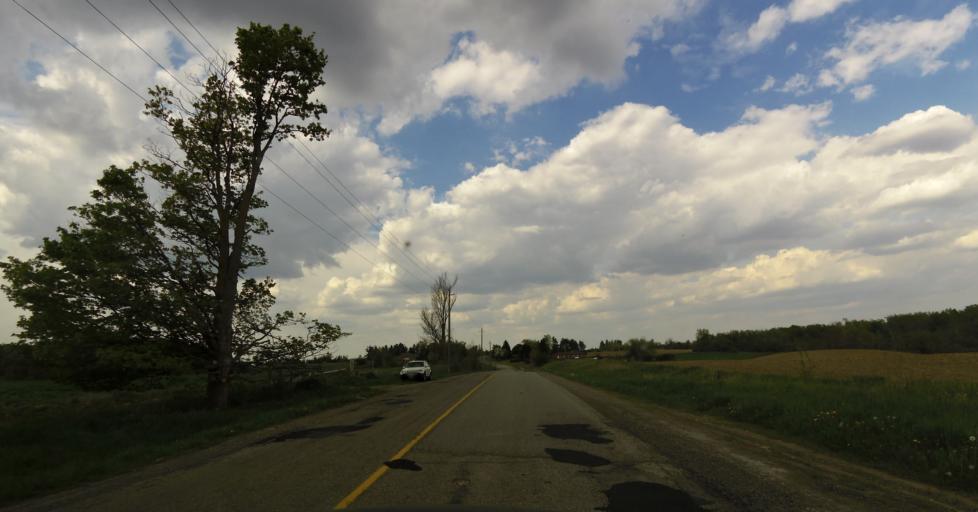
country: CA
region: Ontario
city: Brampton
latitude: 43.7553
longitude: -79.8496
